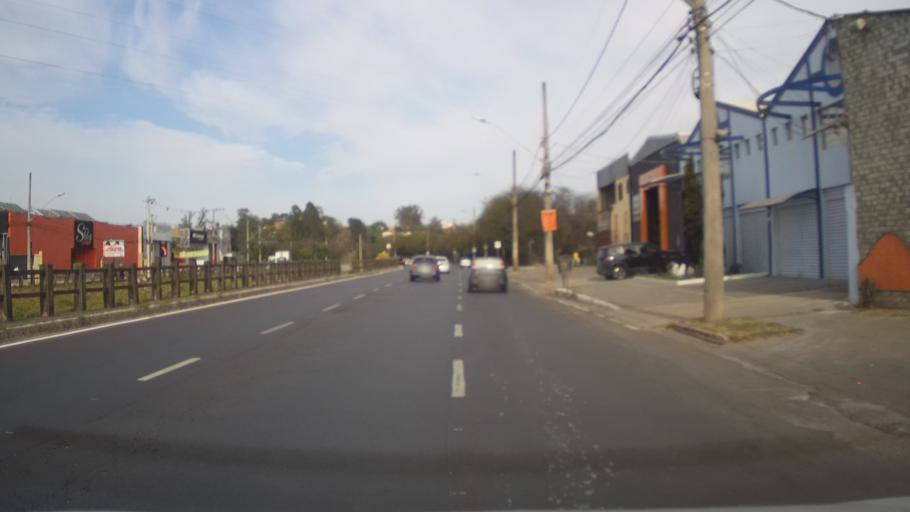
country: BR
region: Minas Gerais
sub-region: Contagem
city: Contagem
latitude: -19.8730
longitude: -44.0220
